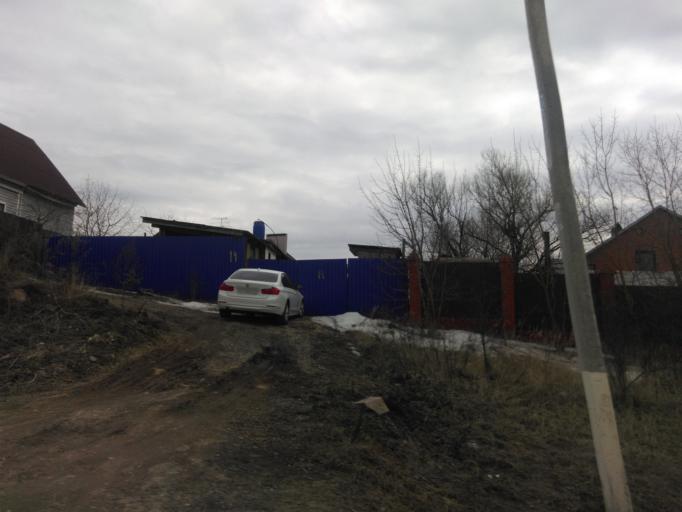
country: RU
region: Moskovskaya
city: Nikolina Gora
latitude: 55.7380
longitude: 36.9722
